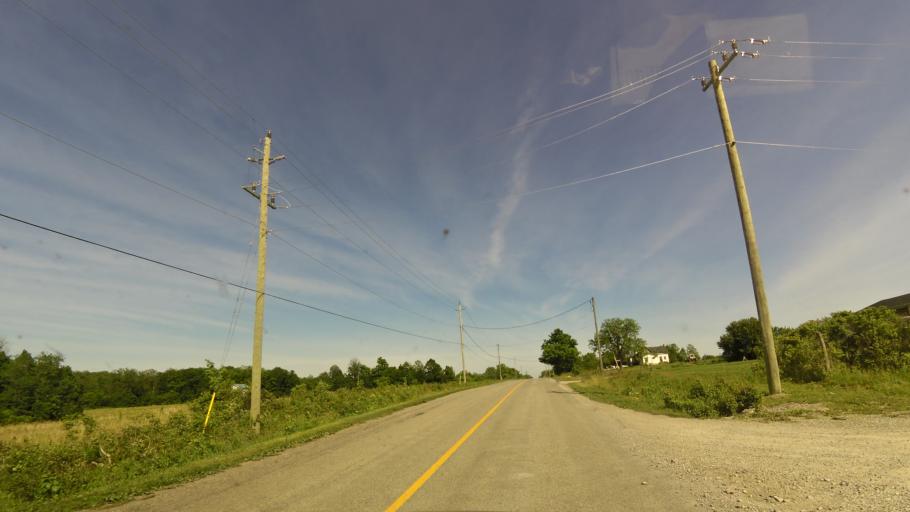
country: CA
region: Ontario
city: Ancaster
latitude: 43.0500
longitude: -80.0112
